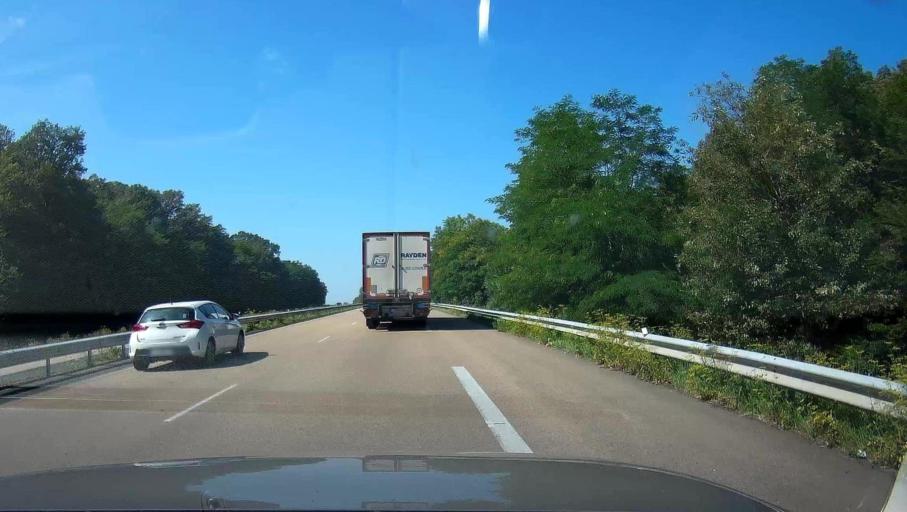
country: FR
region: Champagne-Ardenne
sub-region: Departement de l'Aube
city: Bar-sur-Seine
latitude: 48.1816
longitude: 4.3875
